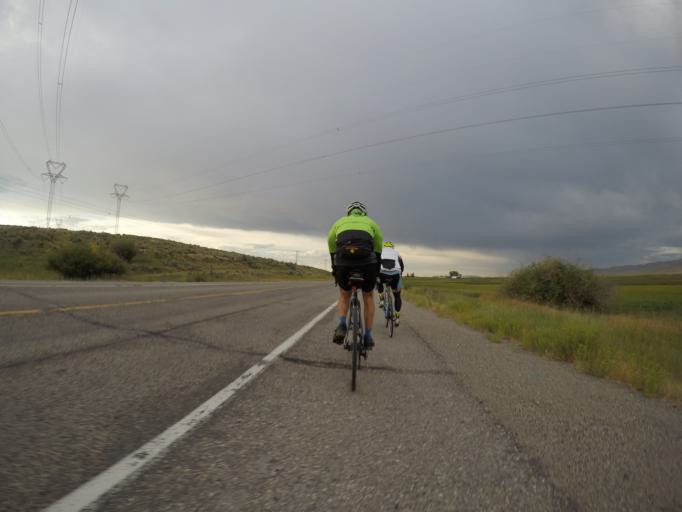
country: US
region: Idaho
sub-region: Bear Lake County
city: Montpelier
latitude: 42.0559
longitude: -110.9315
